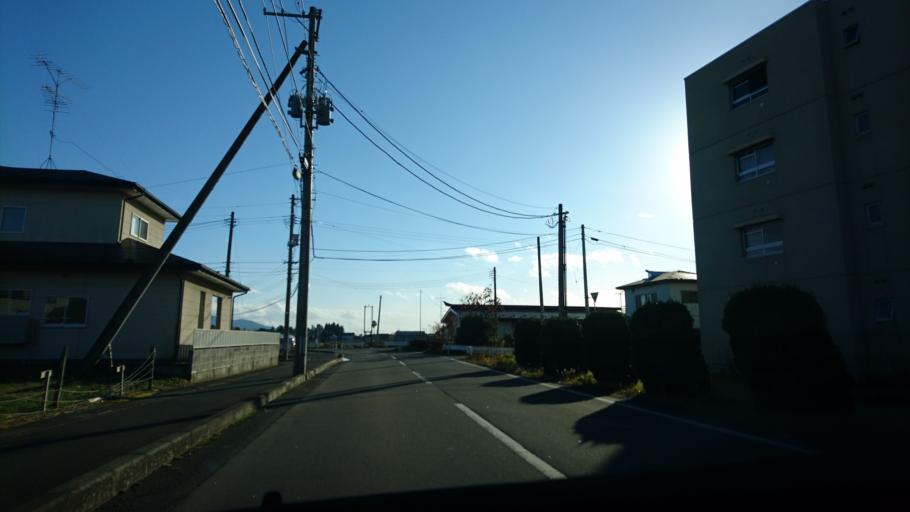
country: JP
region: Iwate
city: Mizusawa
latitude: 39.1138
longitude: 141.1550
